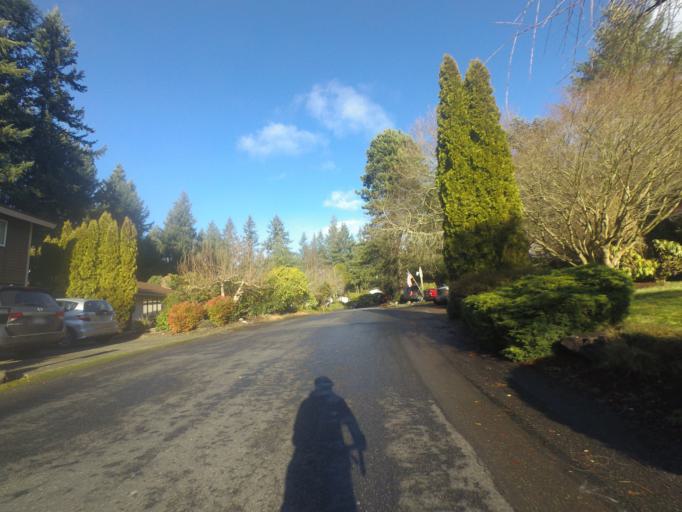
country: US
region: Washington
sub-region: Pierce County
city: University Place
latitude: 47.2122
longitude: -122.5644
